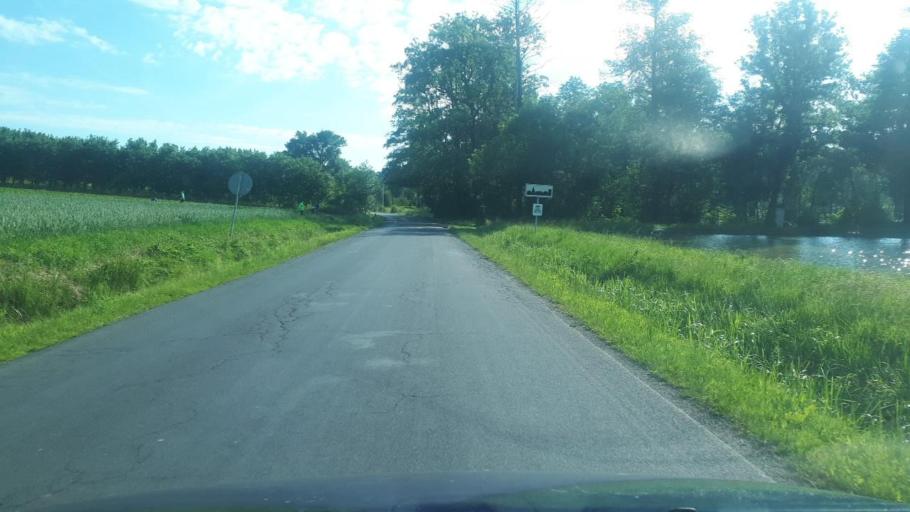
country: PL
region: Silesian Voivodeship
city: Janowice
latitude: 49.9076
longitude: 19.1095
